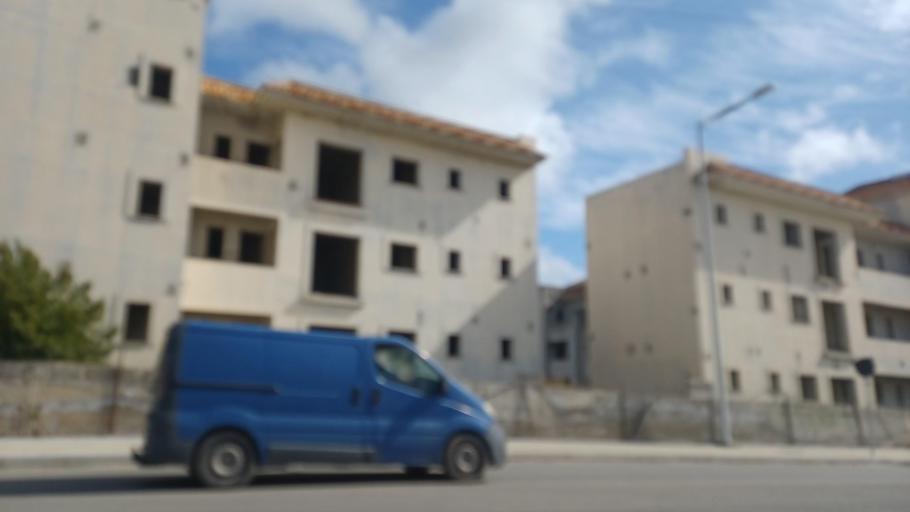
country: CY
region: Pafos
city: Paphos
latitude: 34.7709
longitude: 32.4488
